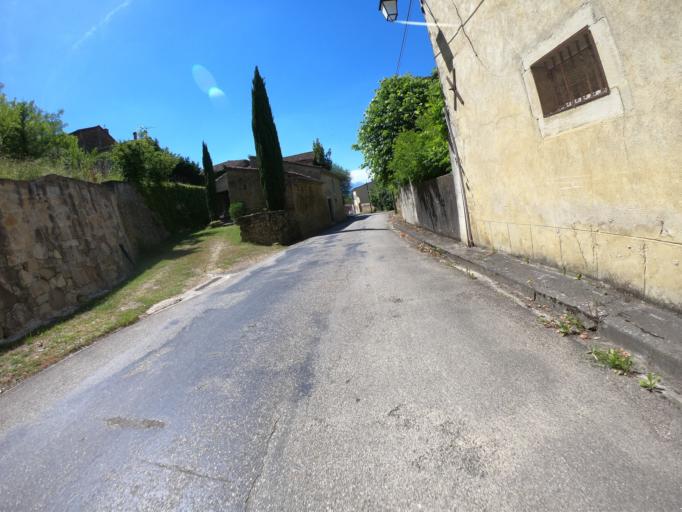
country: FR
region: Midi-Pyrenees
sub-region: Departement de l'Ariege
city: Mirepoix
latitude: 43.0936
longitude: 1.7786
